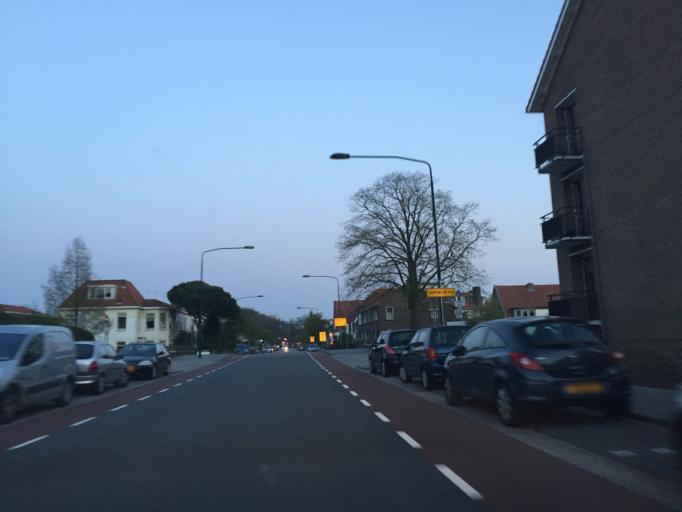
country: NL
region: South Holland
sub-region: Gemeente Leidschendam-Voorburg
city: Voorburg
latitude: 52.0726
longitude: 4.3624
